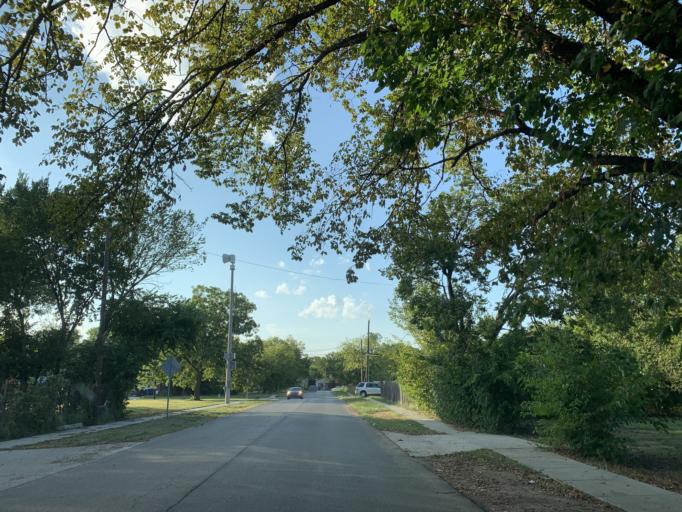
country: US
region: Texas
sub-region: Dallas County
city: Dallas
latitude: 32.7026
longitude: -96.7867
